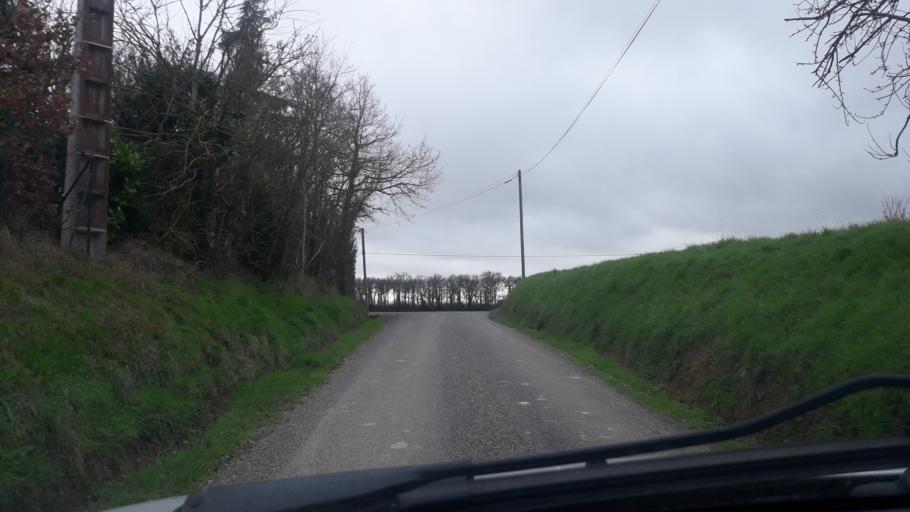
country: FR
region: Midi-Pyrenees
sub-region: Departement du Gers
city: Gimont
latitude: 43.6460
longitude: 0.9742
